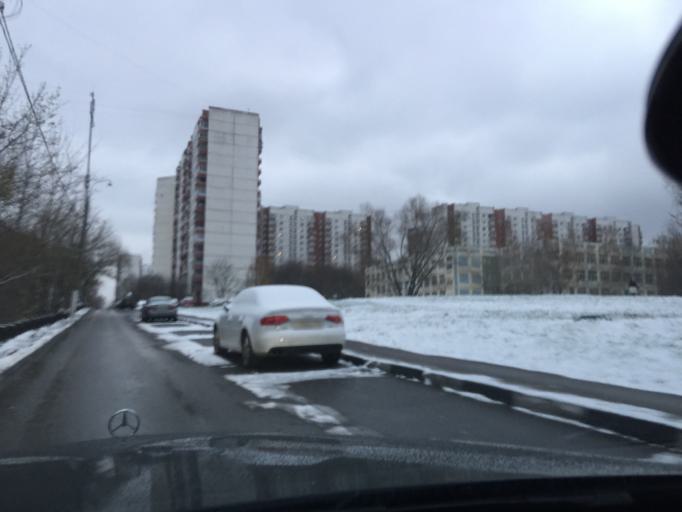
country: RU
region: Moscow
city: Troparevo
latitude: 55.6443
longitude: 37.4849
